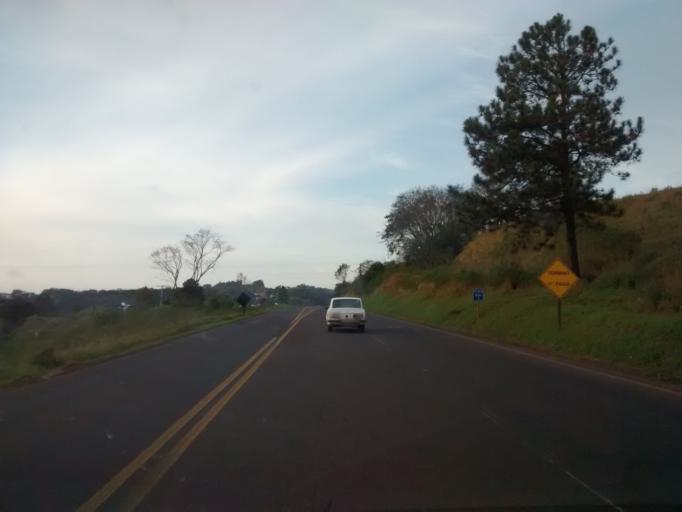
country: BR
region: Parana
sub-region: Francisco Beltrao
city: Francisco Beltrao
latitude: -26.0970
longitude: -53.0606
